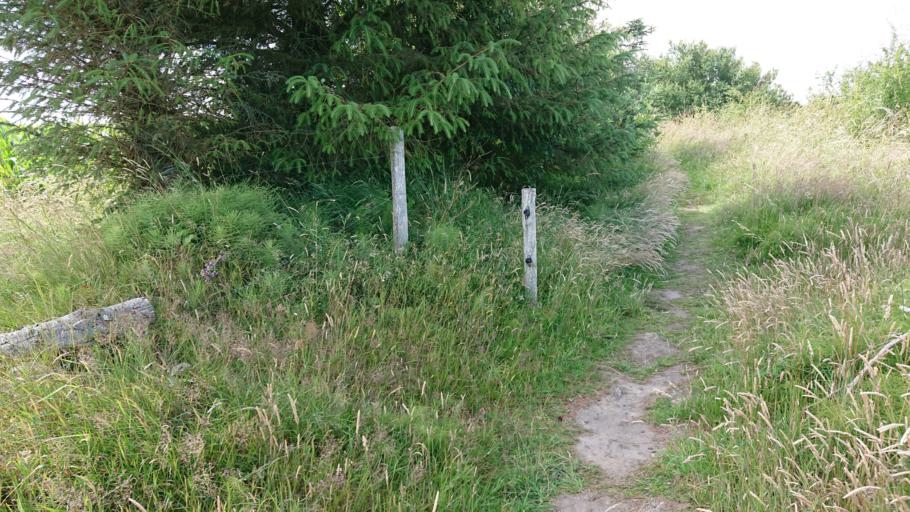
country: DK
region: North Denmark
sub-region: Jammerbugt Kommune
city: Brovst
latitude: 57.1334
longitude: 9.4100
